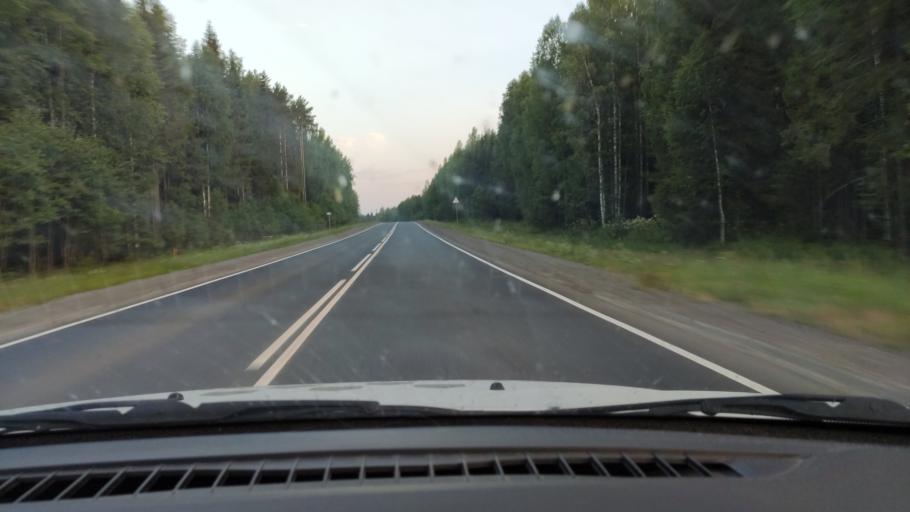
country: RU
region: Perm
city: Zyukayka
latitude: 58.3825
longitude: 54.6064
